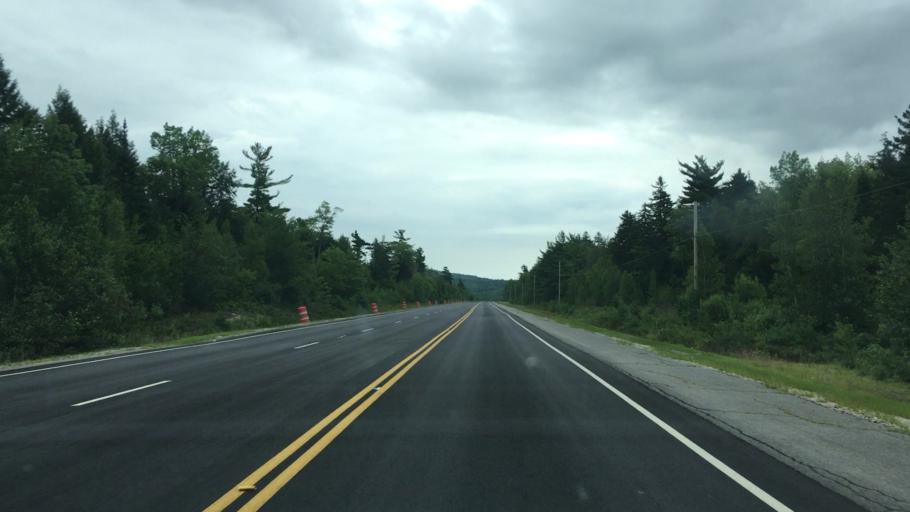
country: US
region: Maine
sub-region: Washington County
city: Cherryfield
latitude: 44.8757
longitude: -67.8919
